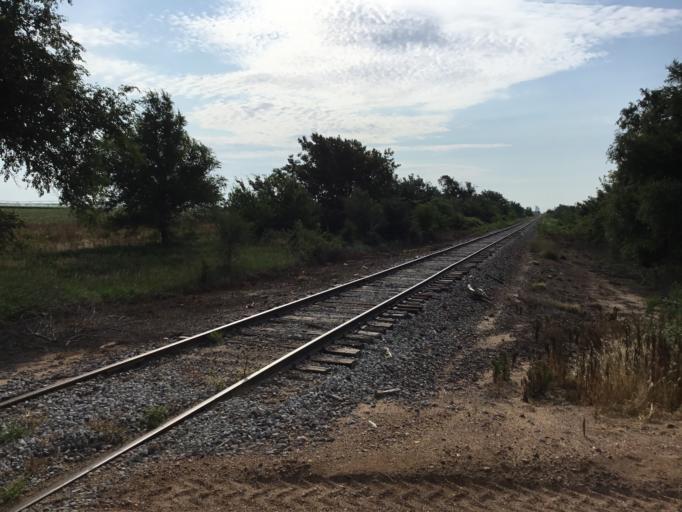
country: US
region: Kansas
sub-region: Barber County
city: Medicine Lodge
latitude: 37.4774
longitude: -98.5926
